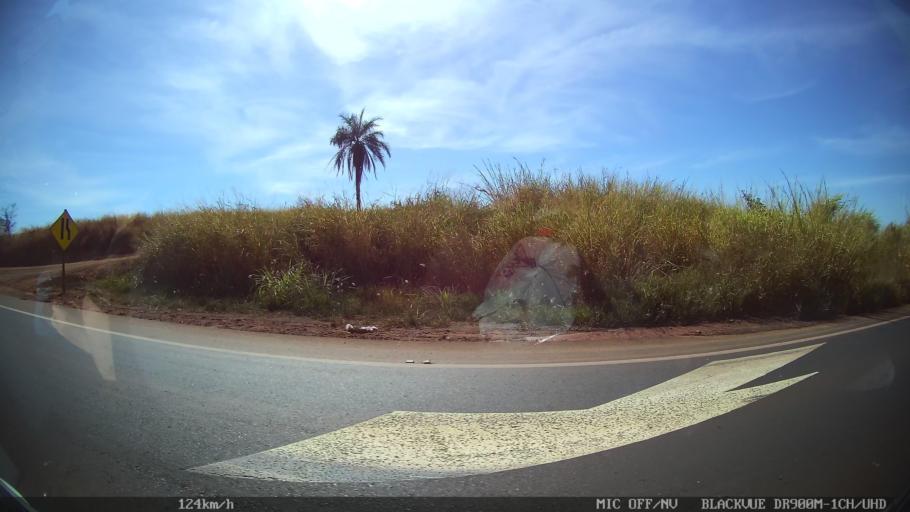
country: BR
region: Sao Paulo
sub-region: Sao Joaquim Da Barra
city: Sao Joaquim da Barra
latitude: -20.5596
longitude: -47.6966
